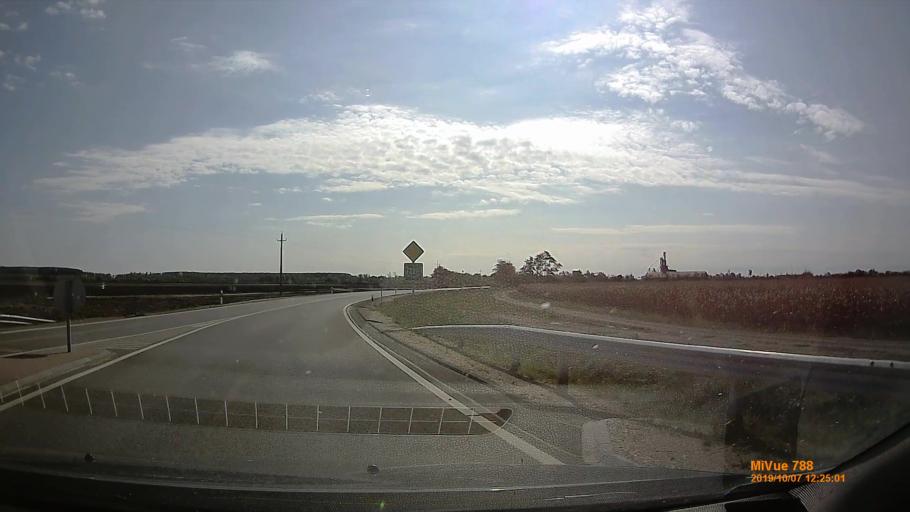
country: HU
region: Jasz-Nagykun-Szolnok
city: Kunszentmarton
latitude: 46.8683
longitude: 20.2651
